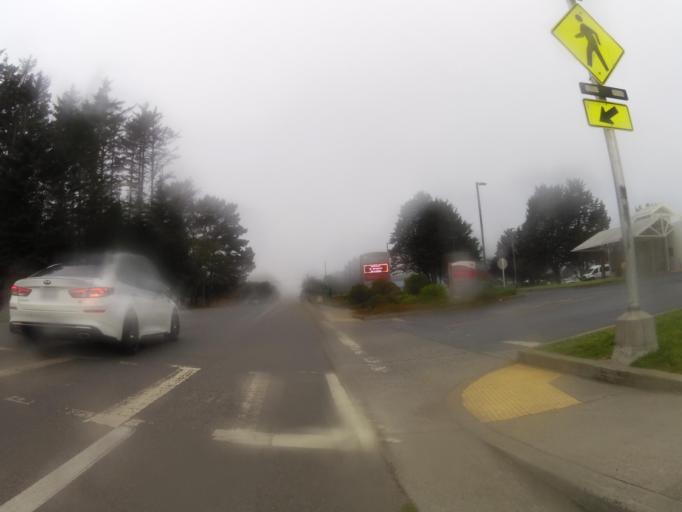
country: US
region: California
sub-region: Del Norte County
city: Crescent City
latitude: 41.7728
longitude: -124.1937
